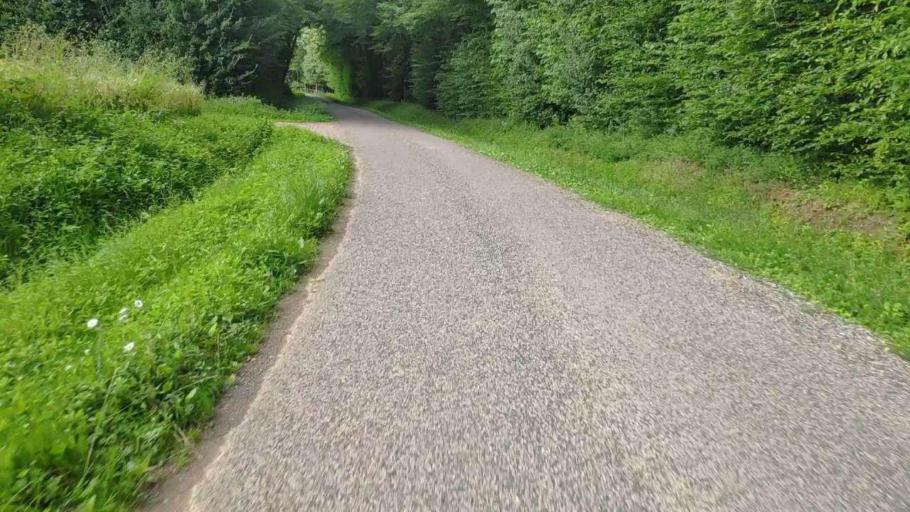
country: FR
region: Franche-Comte
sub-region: Departement du Jura
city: Bletterans
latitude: 46.8353
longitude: 5.5213
